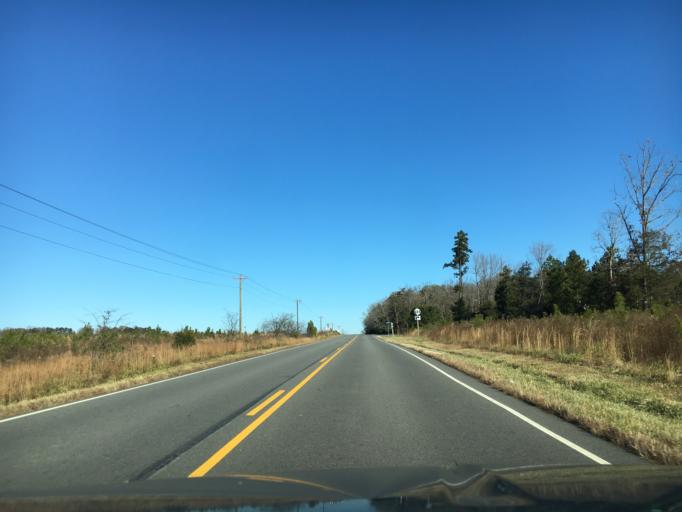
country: US
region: Virginia
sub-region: Buckingham County
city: Buckingham
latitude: 37.5273
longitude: -78.6164
